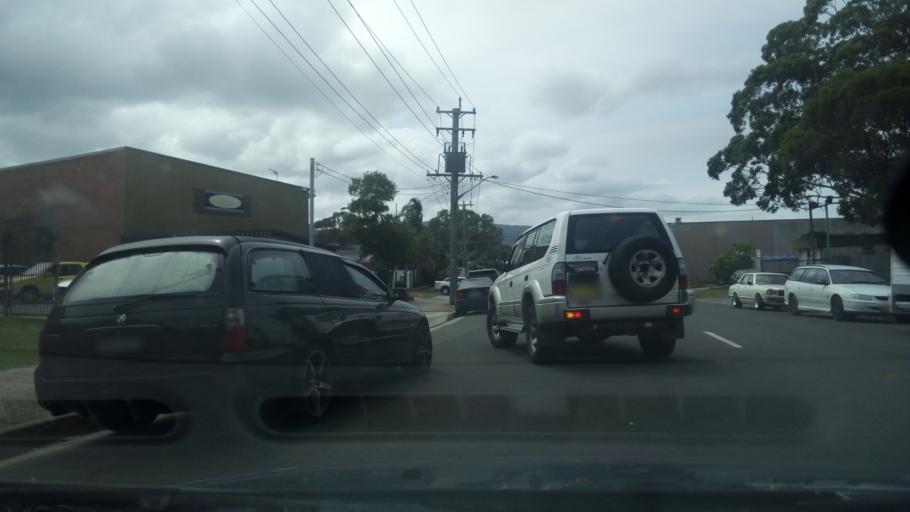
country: AU
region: New South Wales
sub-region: Wollongong
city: Fairy Meadow
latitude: -34.4077
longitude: 150.8951
